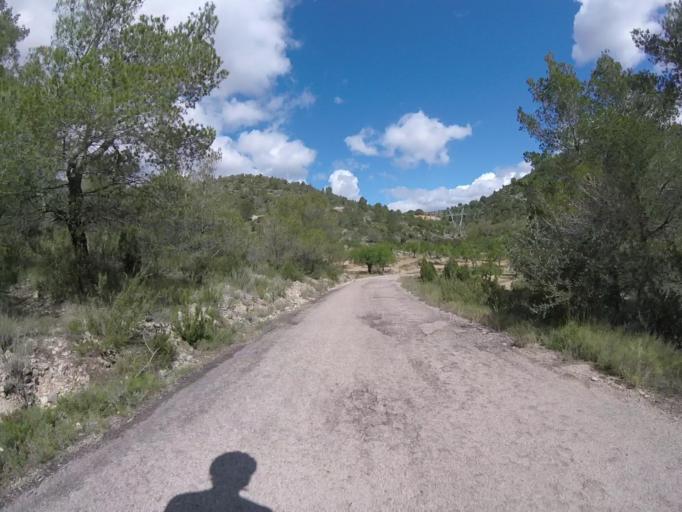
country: ES
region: Valencia
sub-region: Provincia de Castello
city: Adzaneta
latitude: 40.2709
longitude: -0.1088
